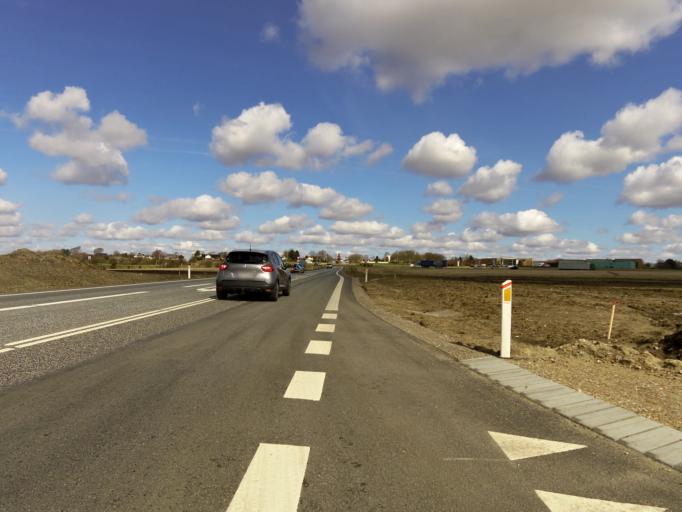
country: DK
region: South Denmark
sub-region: Tonder Kommune
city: Toftlund
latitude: 55.1777
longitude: 9.0608
